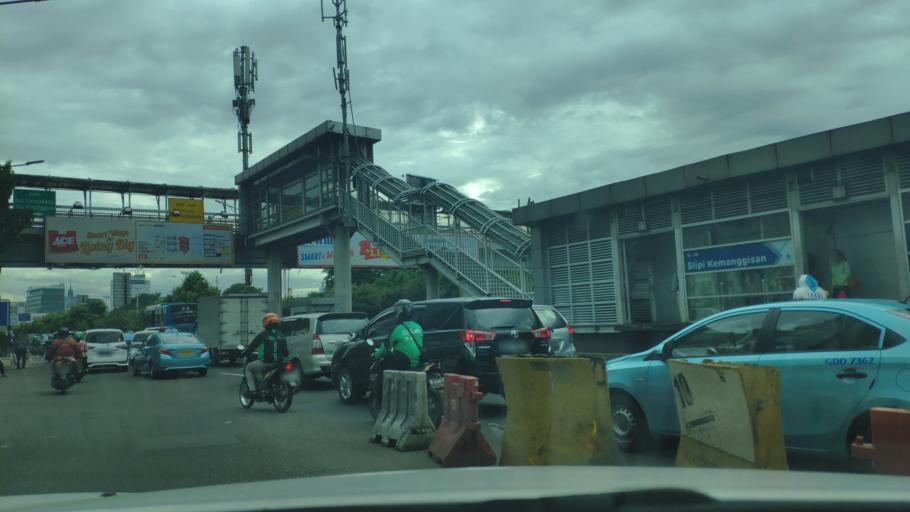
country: ID
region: Jakarta Raya
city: Jakarta
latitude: -6.1898
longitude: 106.7974
